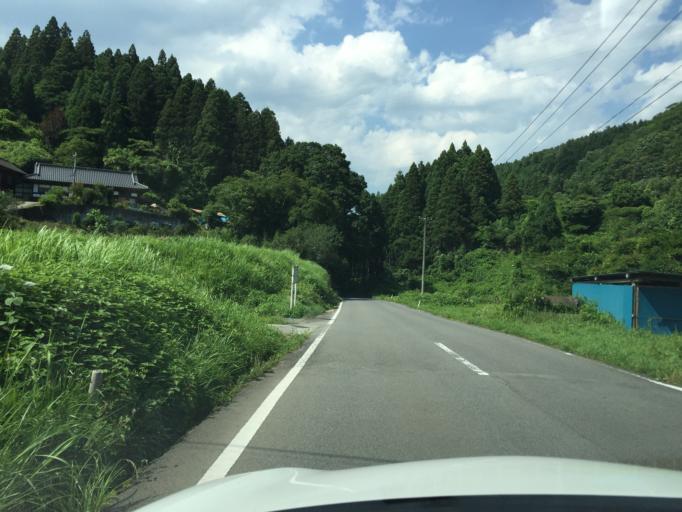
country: JP
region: Fukushima
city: Iwaki
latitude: 36.9943
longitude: 140.7100
